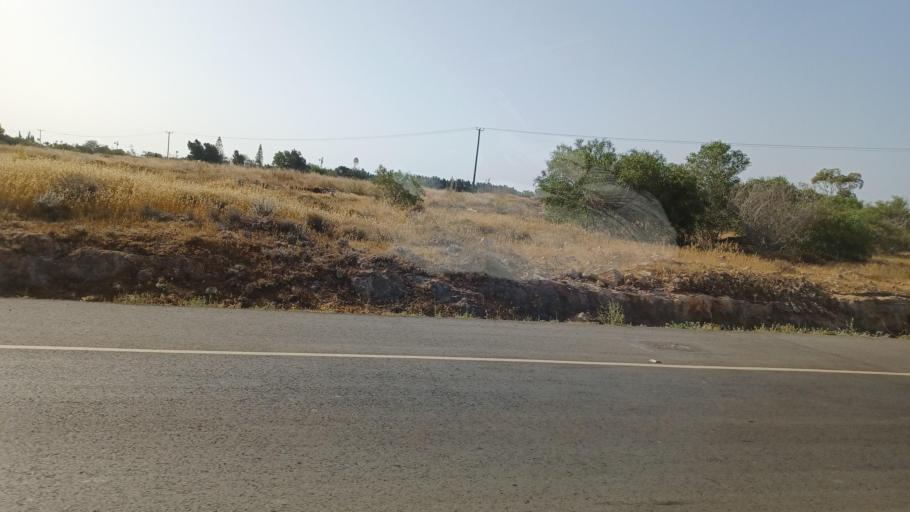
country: CY
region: Ammochostos
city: Liopetri
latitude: 34.9992
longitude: 33.9343
